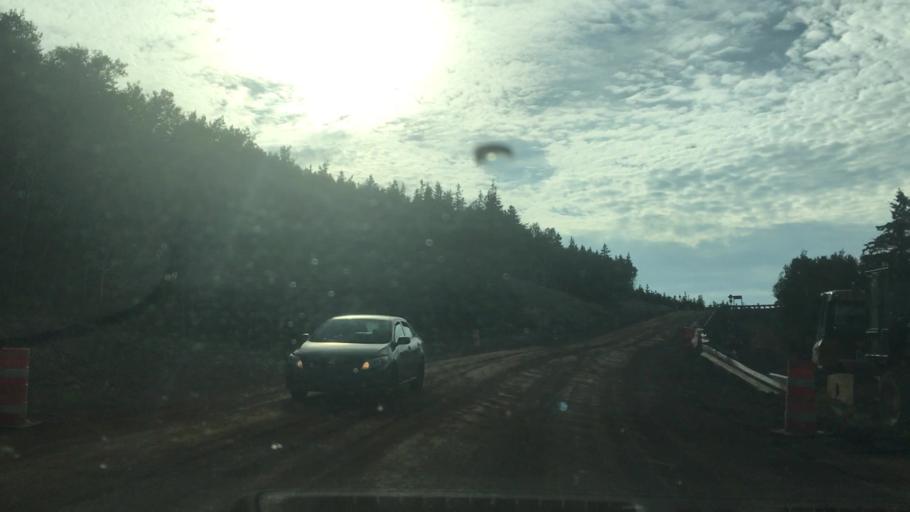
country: CA
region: Nova Scotia
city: Sydney Mines
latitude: 46.8166
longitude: -60.8365
